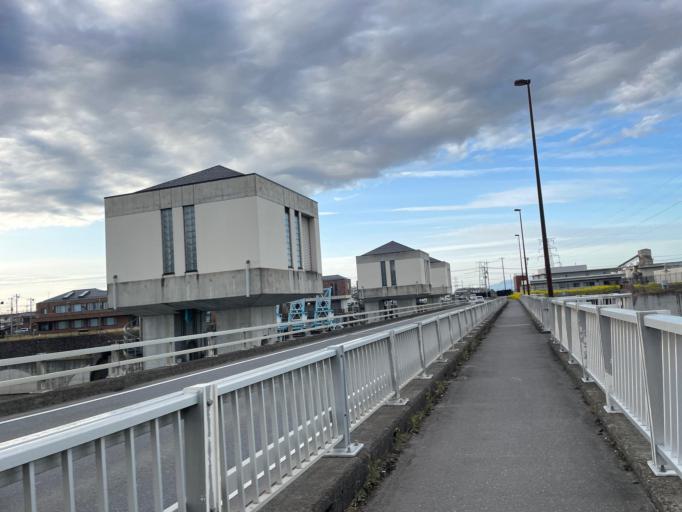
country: JP
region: Saitama
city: Fukayacho
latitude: 36.1331
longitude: 139.2661
